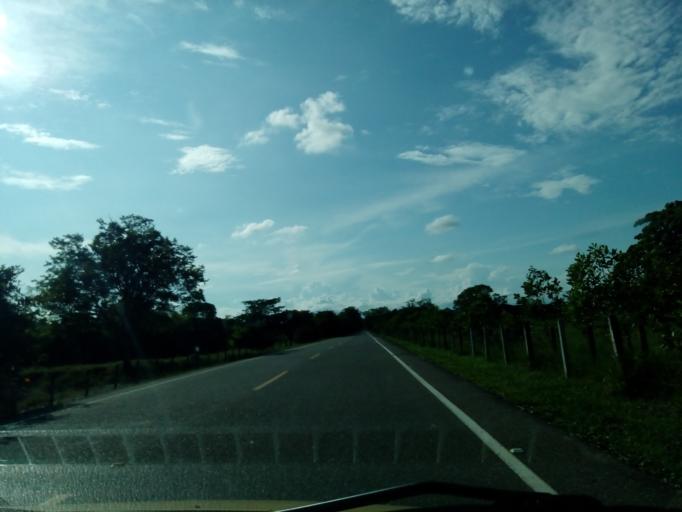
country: CO
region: Boyaca
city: Puerto Boyaca
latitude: 5.9370
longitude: -74.5509
